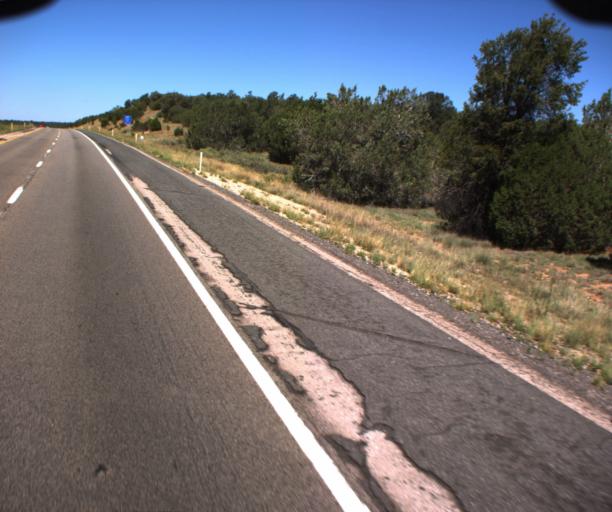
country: US
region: Arizona
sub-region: Mohave County
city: Peach Springs
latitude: 35.2920
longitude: -113.0754
